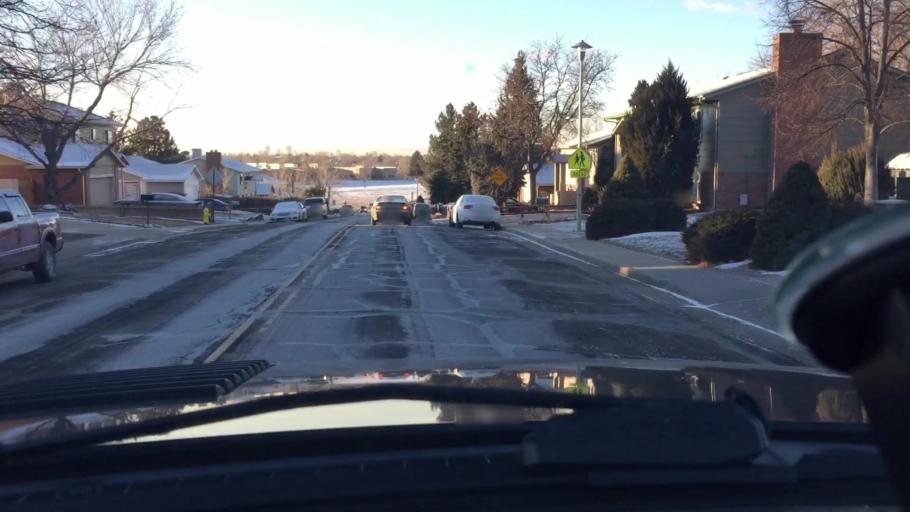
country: US
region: Colorado
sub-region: Adams County
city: Northglenn
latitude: 39.8729
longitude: -105.0056
